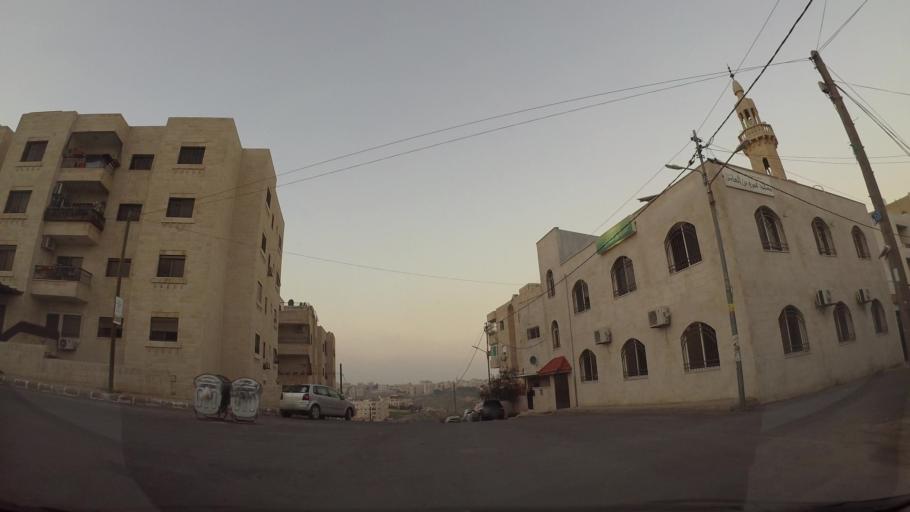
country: JO
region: Amman
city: Amman
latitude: 31.9895
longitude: 35.9682
